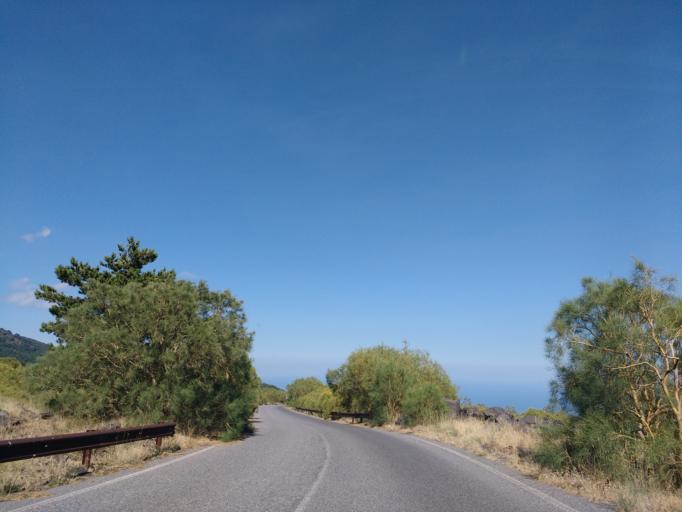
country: IT
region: Sicily
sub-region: Catania
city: Zafferana Etnea
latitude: 37.6959
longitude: 15.0407
